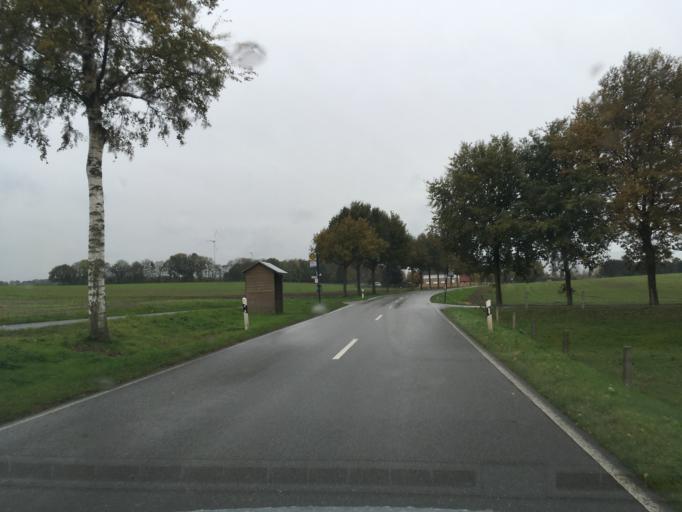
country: DE
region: North Rhine-Westphalia
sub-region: Regierungsbezirk Munster
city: Klein Reken
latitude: 51.8077
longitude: 7.0651
